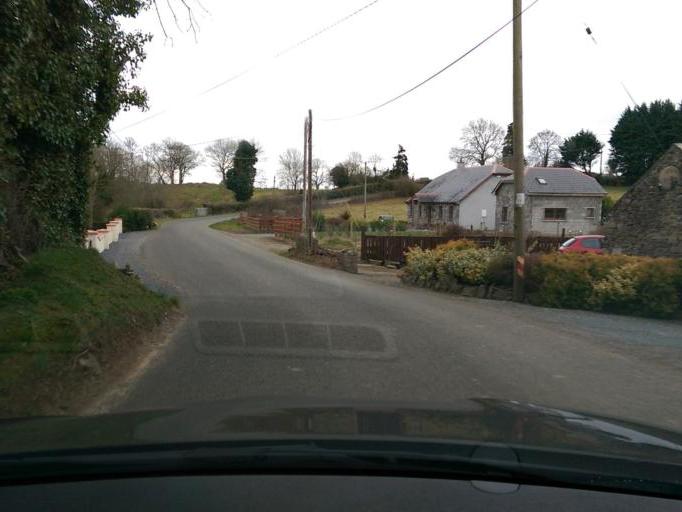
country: IE
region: Leinster
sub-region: An Iarmhi
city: Moate
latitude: 53.3863
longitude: -7.8241
